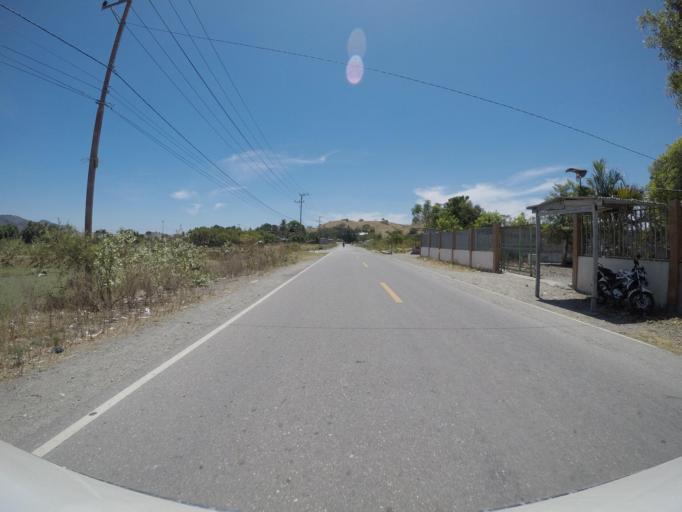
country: TL
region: Manatuto
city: Manatuto
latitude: -8.5301
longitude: 126.0048
